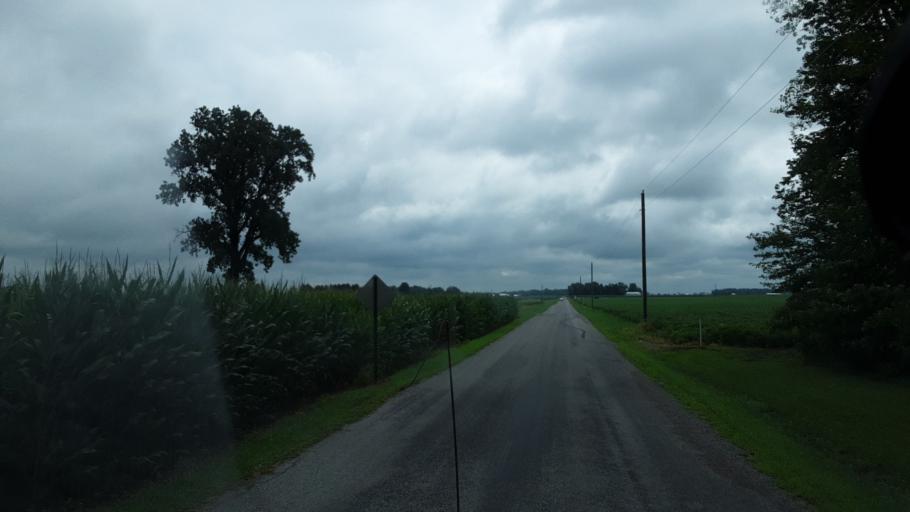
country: US
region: Indiana
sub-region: Wells County
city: Ossian
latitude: 40.8593
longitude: -85.1077
